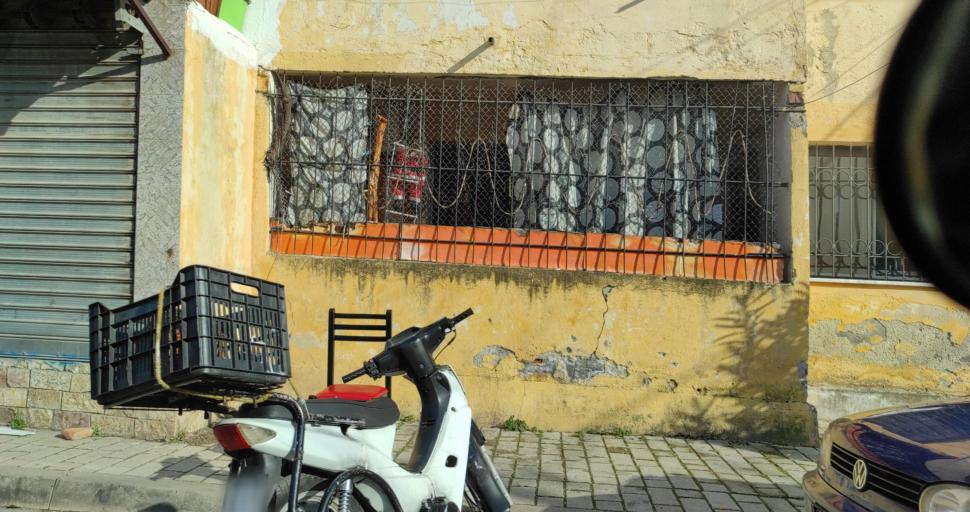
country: AL
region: Lezhe
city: Lezhe
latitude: 41.7859
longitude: 19.6441
